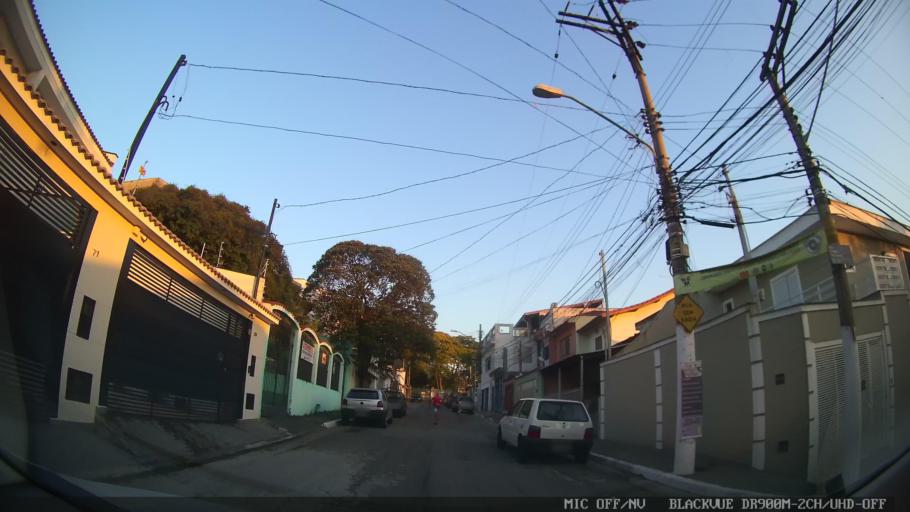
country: BR
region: Sao Paulo
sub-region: Sao Paulo
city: Sao Paulo
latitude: -23.4957
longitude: -46.6404
